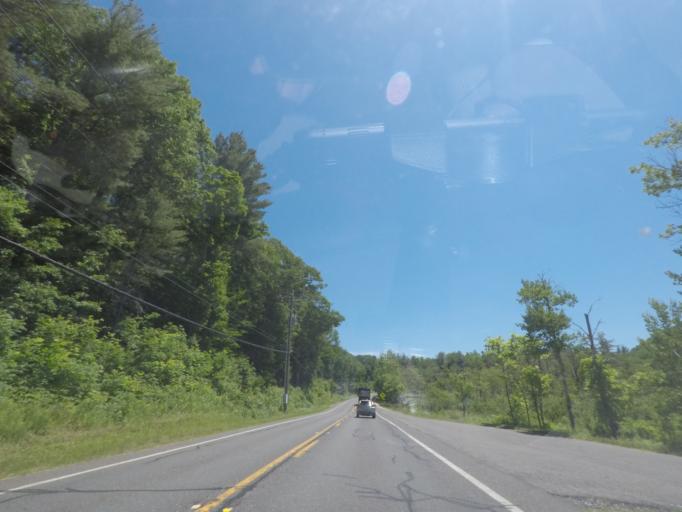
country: US
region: Massachusetts
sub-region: Berkshire County
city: Becket
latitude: 42.2925
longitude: -73.1598
